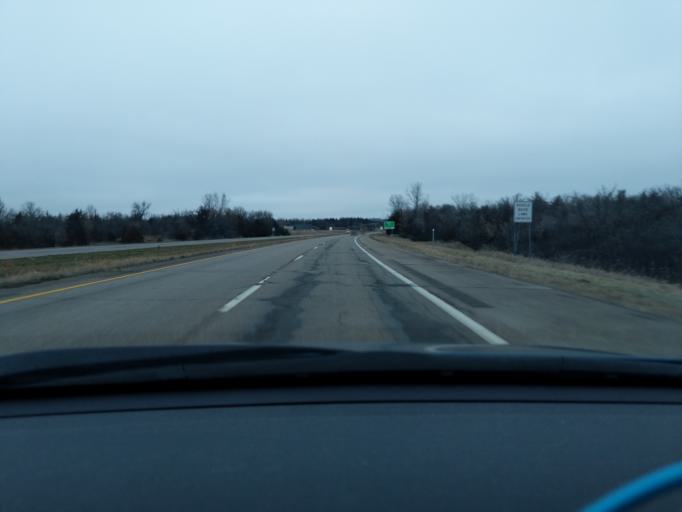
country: US
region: Minnesota
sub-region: Yellow Medicine County
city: Granite Falls
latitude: 44.7975
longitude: -95.5482
